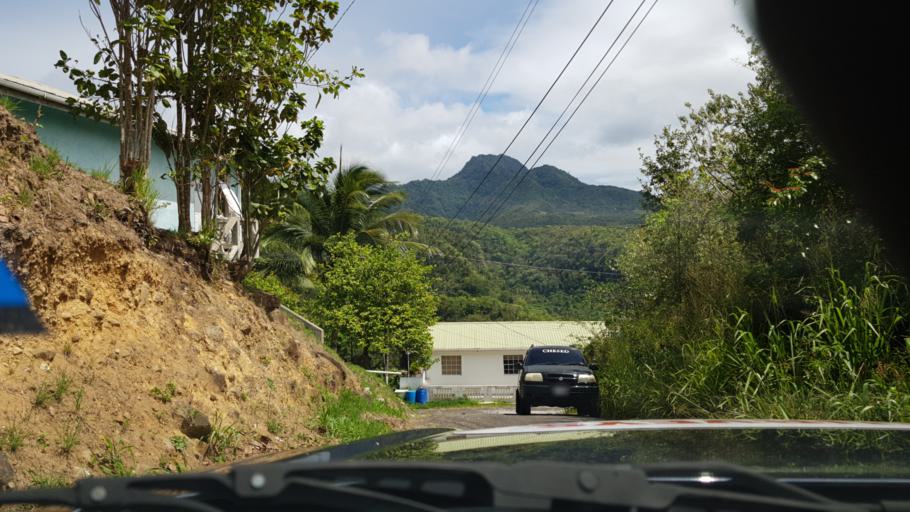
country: LC
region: Anse-la-Raye
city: Anse La Raye
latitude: 13.9445
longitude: -61.0396
